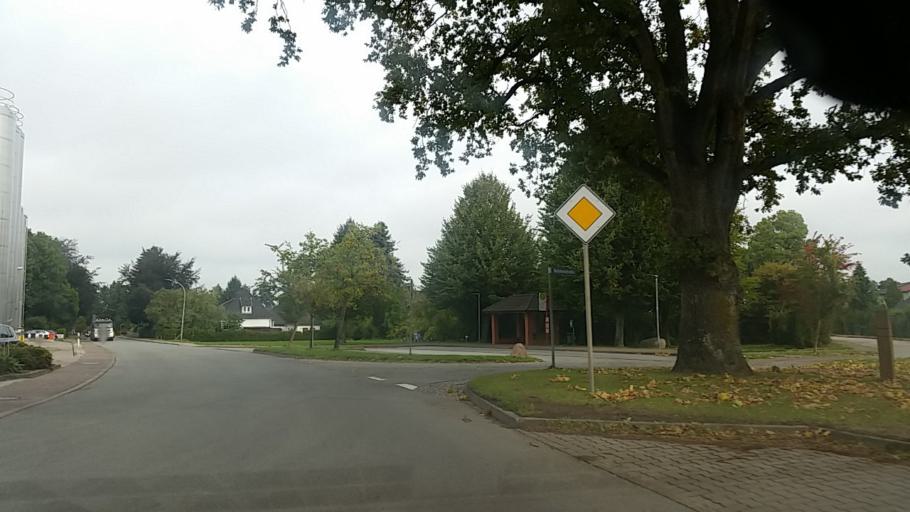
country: DE
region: Schleswig-Holstein
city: Schmalfeld
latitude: 53.8739
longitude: 9.9858
